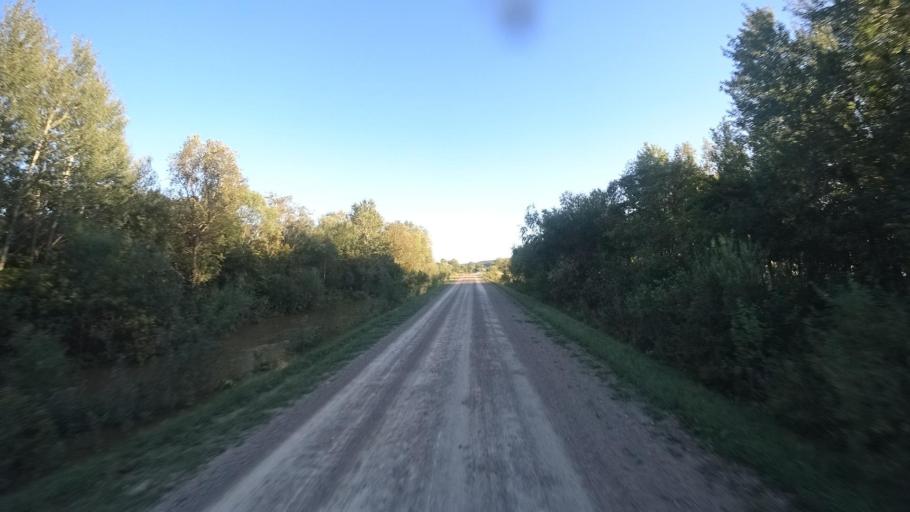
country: RU
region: Primorskiy
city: Kirovskiy
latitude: 44.7821
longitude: 133.6256
